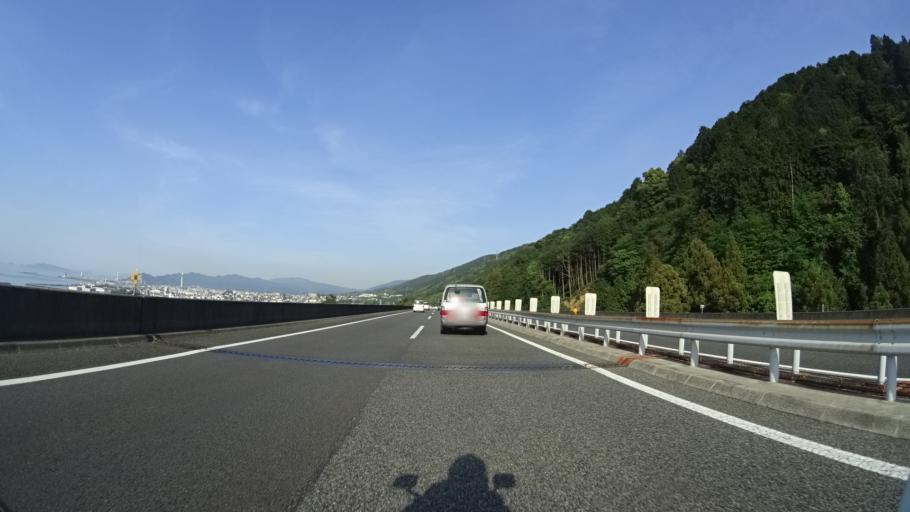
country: JP
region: Ehime
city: Kawanoecho
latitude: 33.9607
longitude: 133.5066
